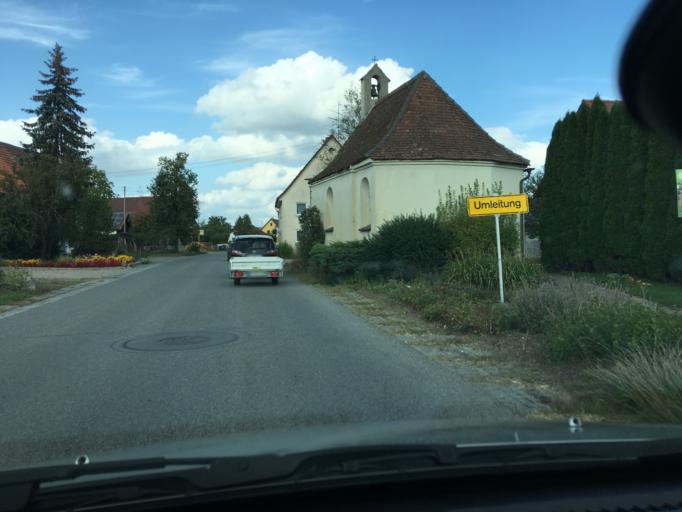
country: DE
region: Baden-Wuerttemberg
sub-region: Tuebingen Region
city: Hochdorf
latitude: 48.0428
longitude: 9.7980
